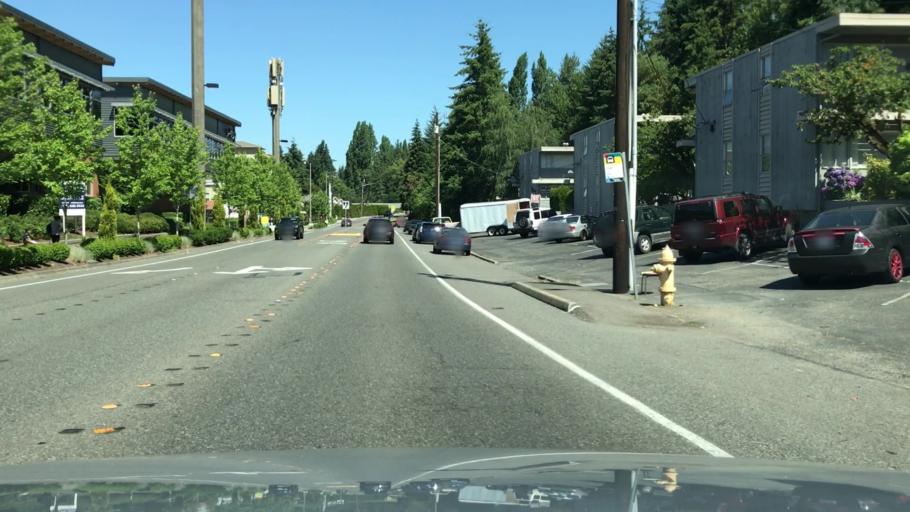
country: US
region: Washington
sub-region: King County
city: Eastgate
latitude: 47.6037
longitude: -122.1309
